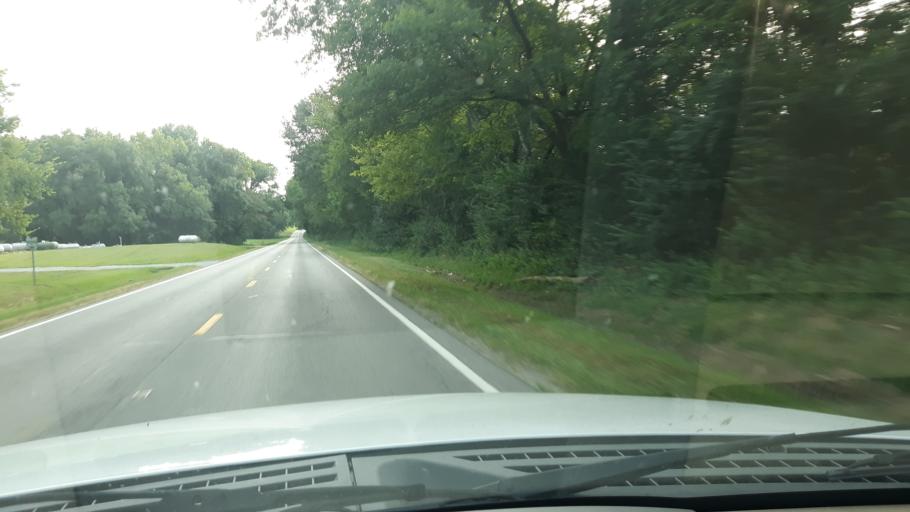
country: US
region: Illinois
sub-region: Wabash County
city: Mount Carmel
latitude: 38.3982
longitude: -87.7982
